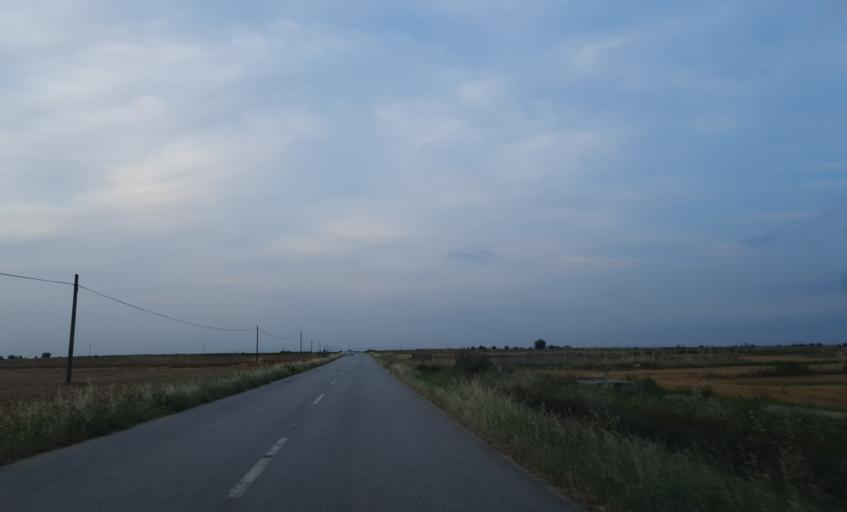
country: TR
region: Kirklareli
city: Buyukkaristiran
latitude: 41.3186
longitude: 27.6053
